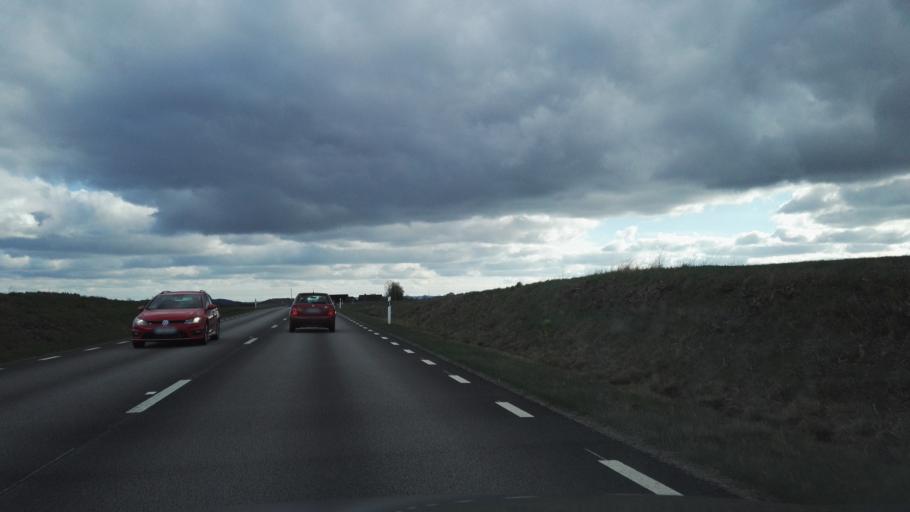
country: SE
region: Skane
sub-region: Sjobo Kommun
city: Sjoebo
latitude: 55.6708
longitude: 13.7144
